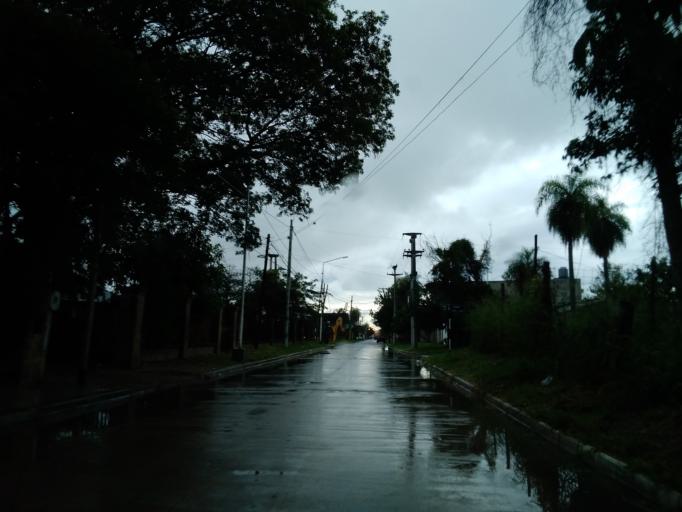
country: AR
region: Corrientes
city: Corrientes
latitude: -27.4979
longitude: -58.8210
